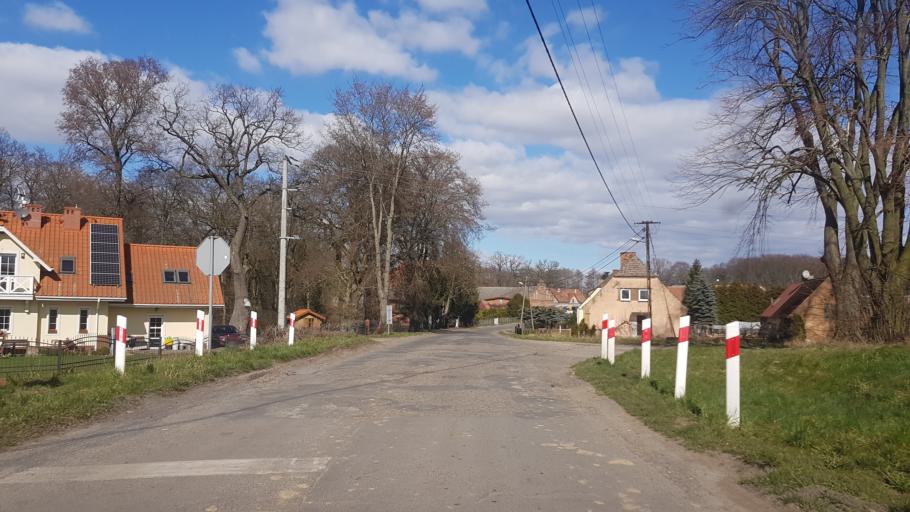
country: PL
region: West Pomeranian Voivodeship
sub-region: Powiat stargardzki
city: Marianowo
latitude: 53.3358
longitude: 15.1930
